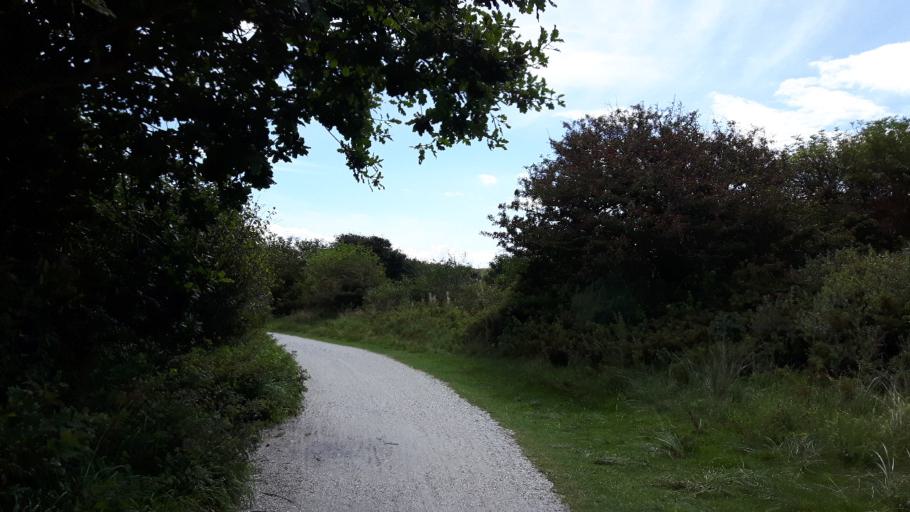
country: NL
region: Friesland
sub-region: Gemeente Ameland
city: Hollum
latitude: 53.4411
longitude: 5.6199
